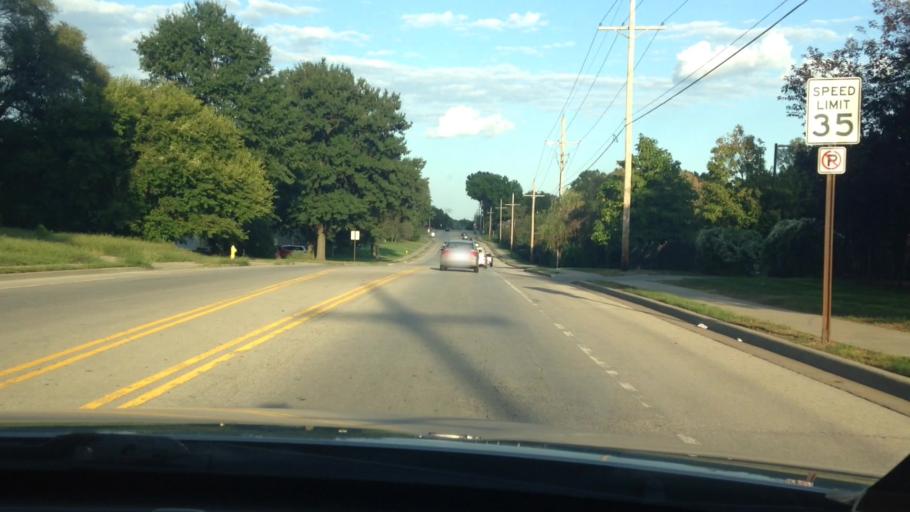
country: US
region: Missouri
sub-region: Jackson County
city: Raytown
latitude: 38.9662
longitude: -94.4923
